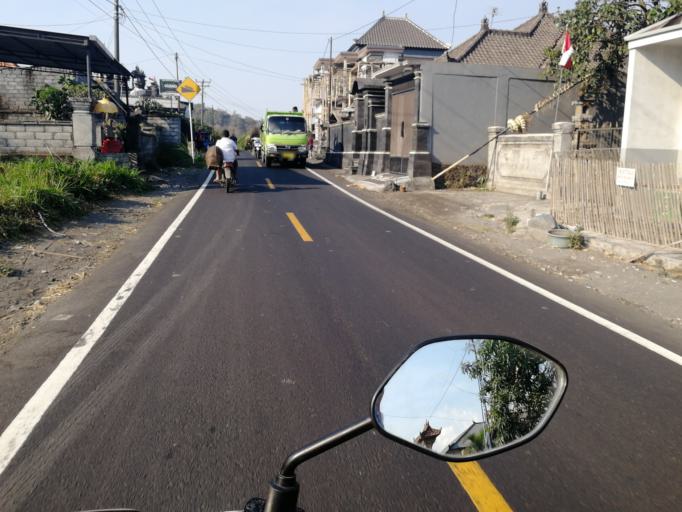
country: ID
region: Bali
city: Banjar Trunyan
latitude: -8.2458
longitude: 115.4001
